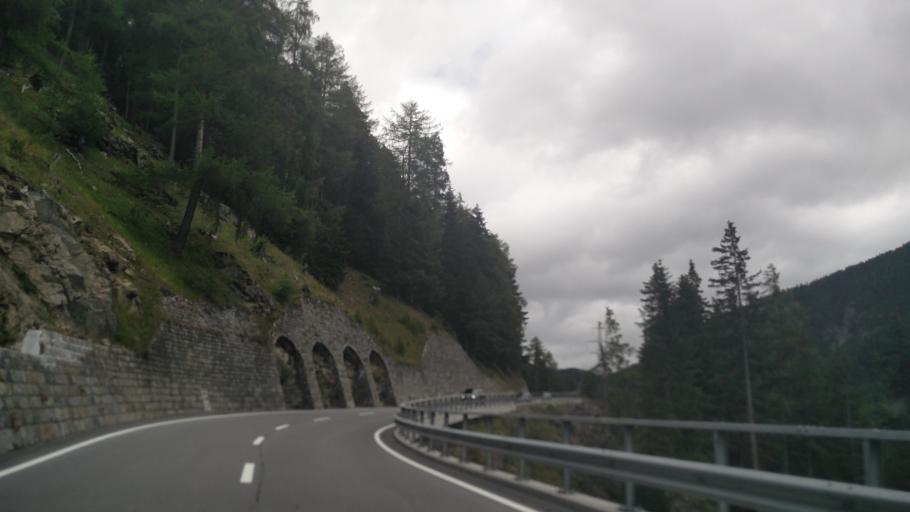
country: CH
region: Grisons
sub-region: Inn District
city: Zernez
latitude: 46.6955
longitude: 10.1180
